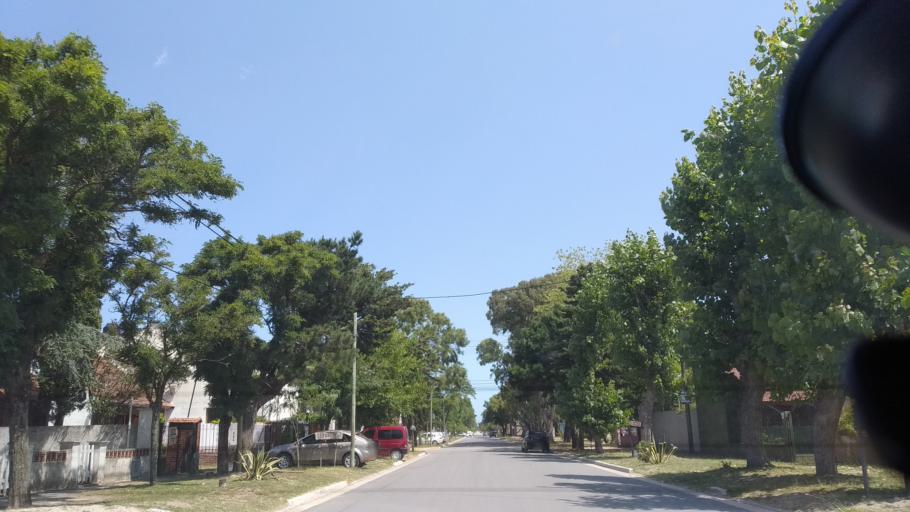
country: AR
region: Buenos Aires
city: Mar del Tuyu
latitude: -36.5768
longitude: -56.6937
